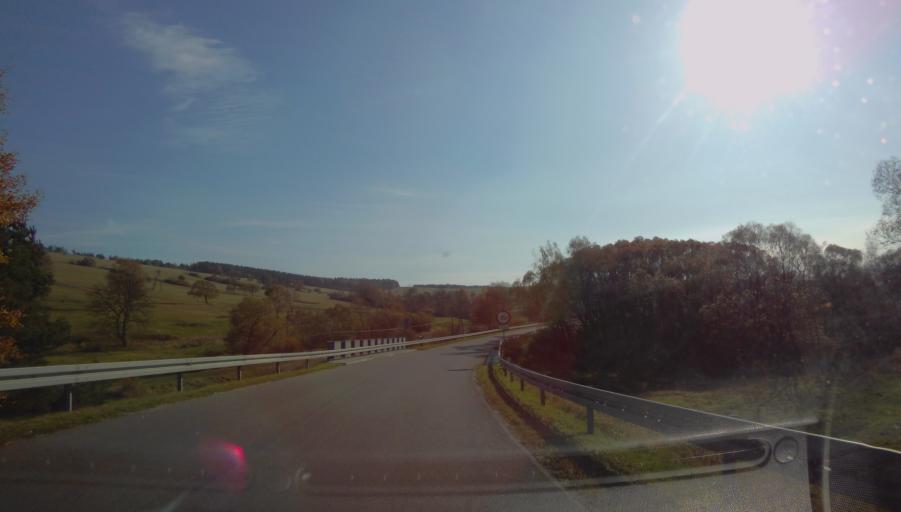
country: PL
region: Subcarpathian Voivodeship
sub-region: Powiat sanocki
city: Komancza
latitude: 49.2832
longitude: 22.0746
